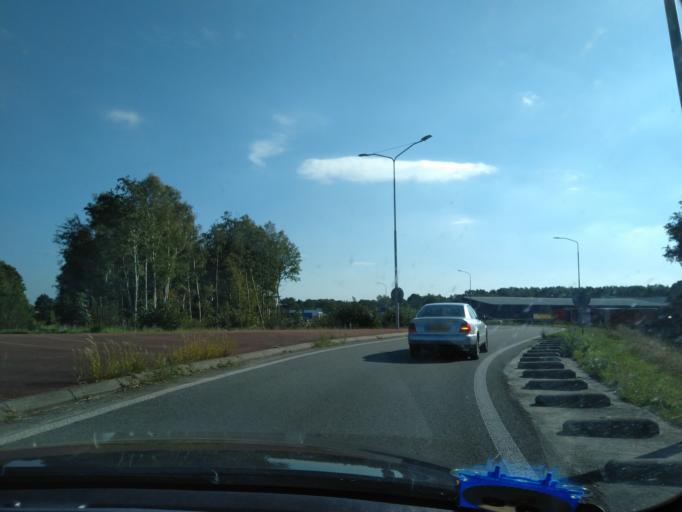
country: NL
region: Groningen
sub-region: Gemeente Pekela
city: Oude Pekela
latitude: 53.0871
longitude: 6.9629
